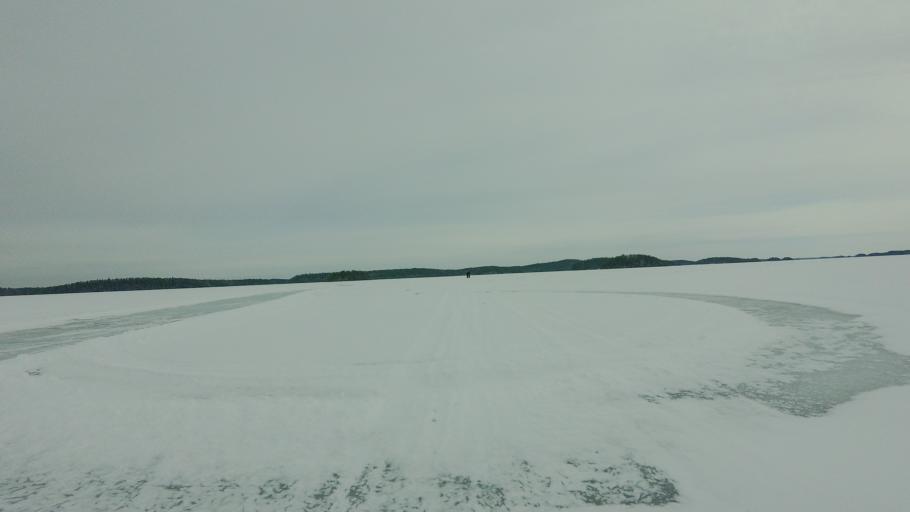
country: FI
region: Southern Savonia
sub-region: Savonlinna
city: Rantasalmi
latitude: 62.1029
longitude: 28.4472
